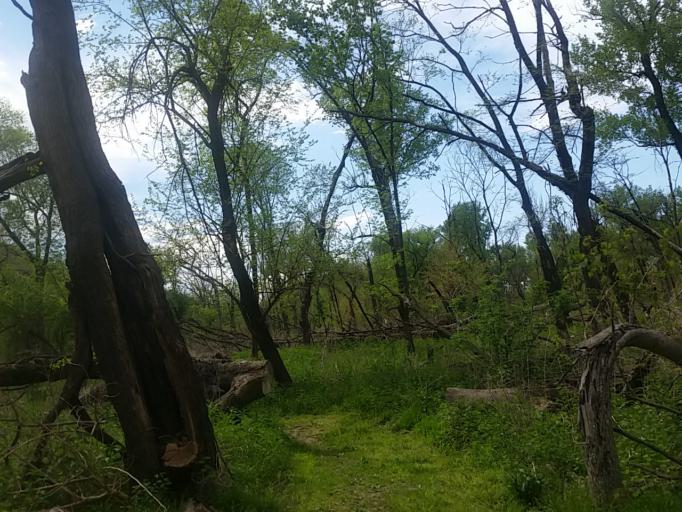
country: US
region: Nebraska
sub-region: Sarpy County
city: Bellevue
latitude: 41.1806
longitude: -95.8995
